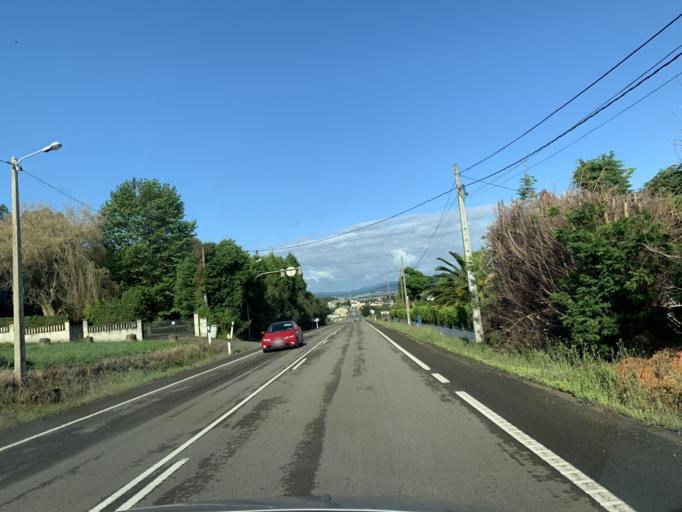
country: ES
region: Galicia
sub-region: Provincia de Lugo
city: Barreiros
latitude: 43.5427
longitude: -7.1767
